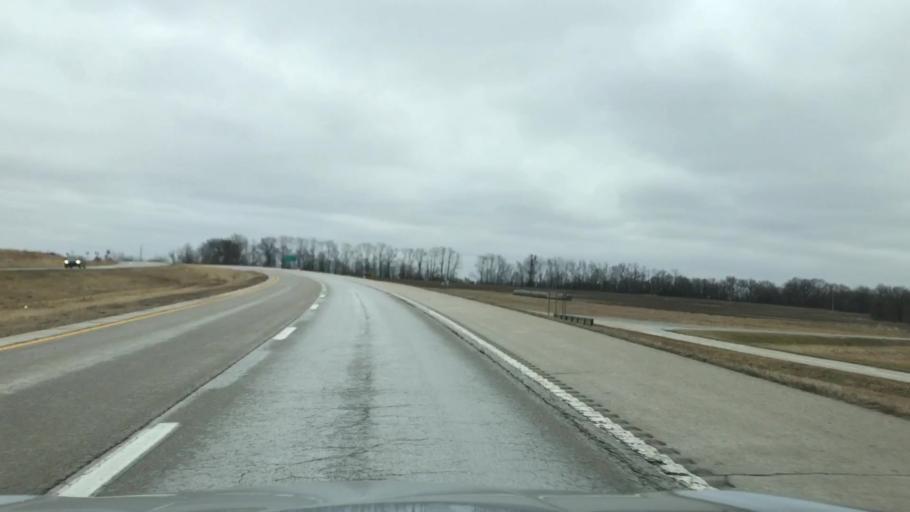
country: US
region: Missouri
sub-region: Livingston County
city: Chillicothe
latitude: 39.7368
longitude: -93.6329
